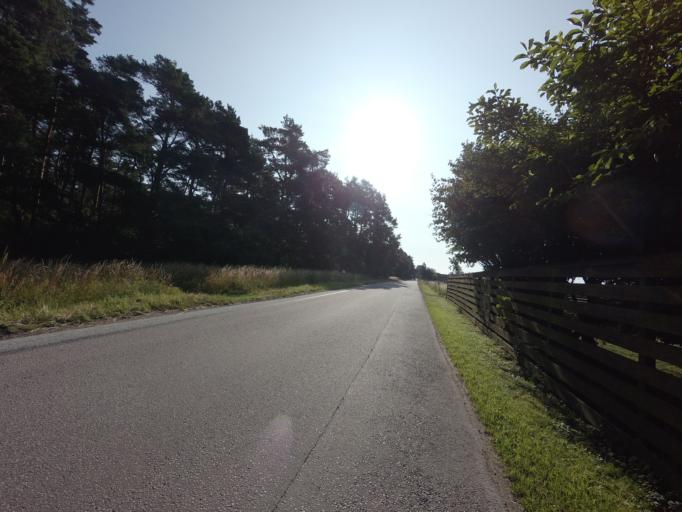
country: SE
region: Skane
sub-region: Kavlinge Kommun
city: Hofterup
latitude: 55.8324
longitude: 12.9527
